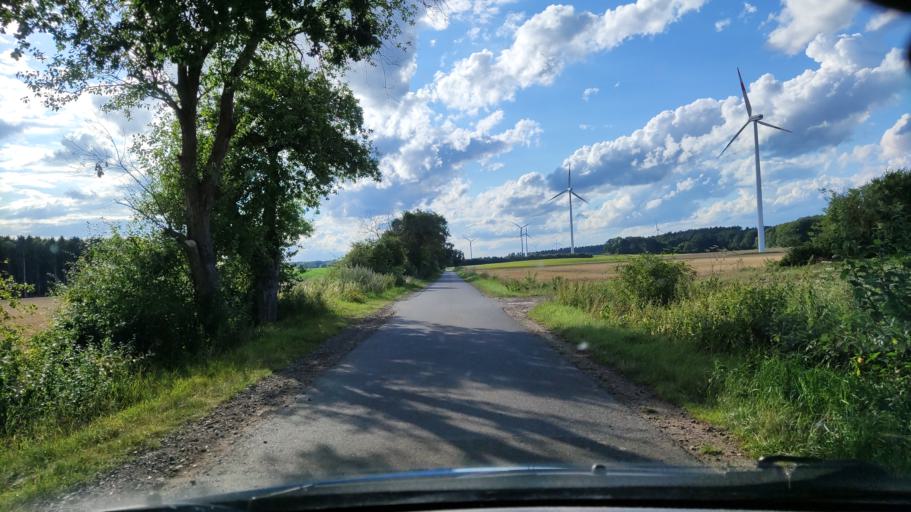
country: DE
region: Lower Saxony
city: Nahrendorf
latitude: 53.1752
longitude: 10.8072
